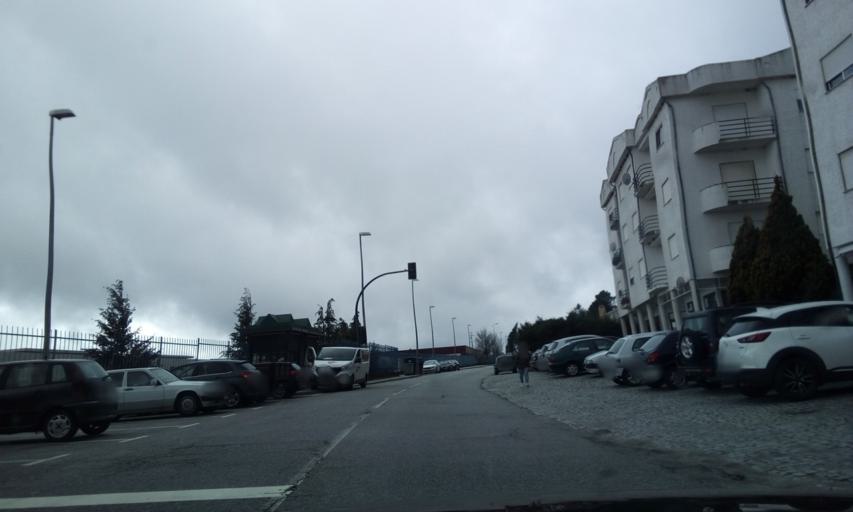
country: PT
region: Guarda
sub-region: Fornos de Algodres
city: Fornos de Algodres
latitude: 40.6162
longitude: -7.5444
